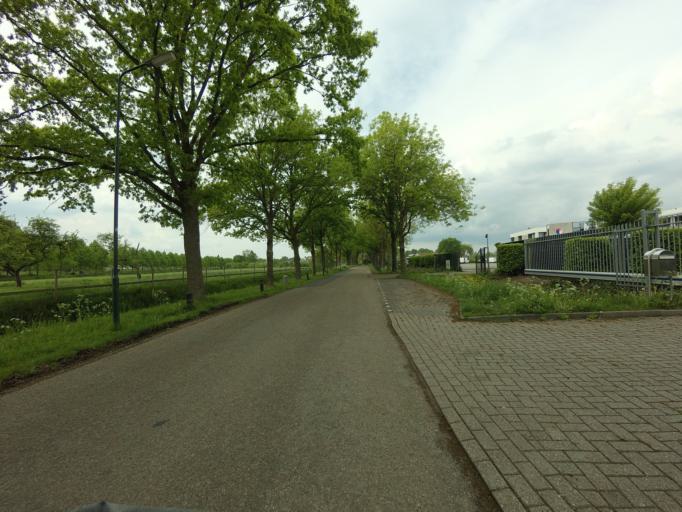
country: NL
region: Utrecht
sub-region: Gemeente Oudewater
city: Oudewater
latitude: 52.0216
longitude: 4.8794
